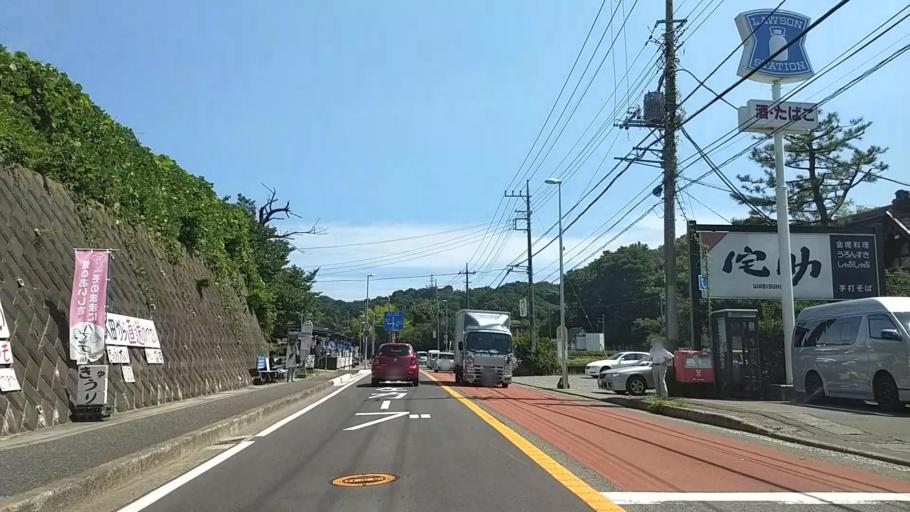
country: JP
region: Kanagawa
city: Fujisawa
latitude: 35.3672
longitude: 139.5188
